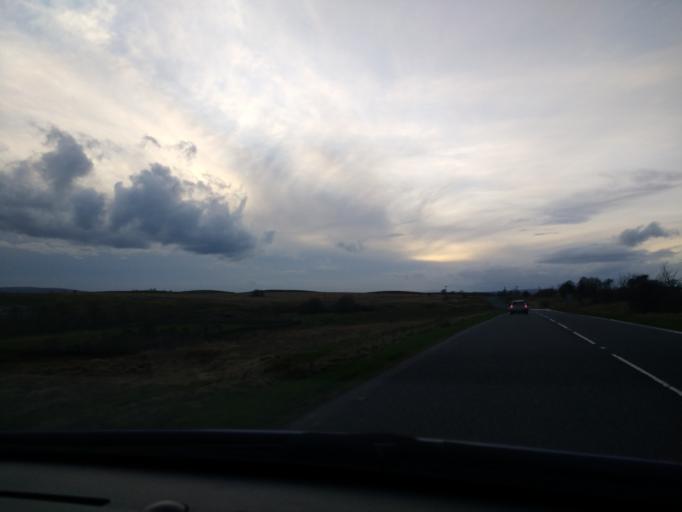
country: GB
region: England
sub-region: North Yorkshire
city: Ingleton
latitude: 54.1260
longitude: -2.4338
